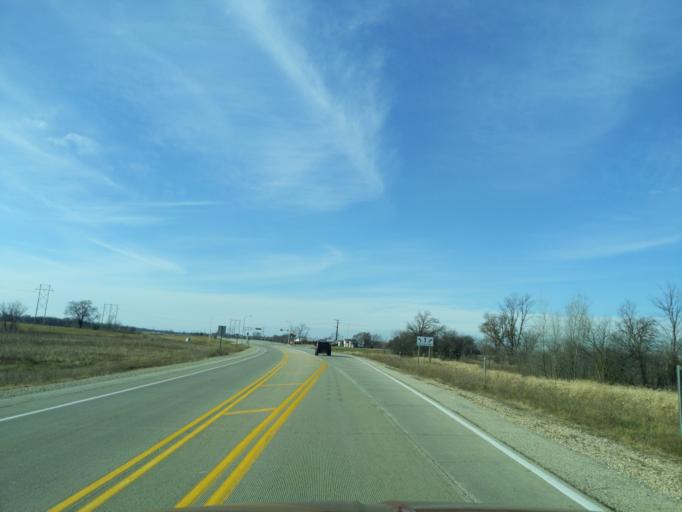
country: US
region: Wisconsin
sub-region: Walworth County
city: Whitewater
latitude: 42.8195
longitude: -88.6976
